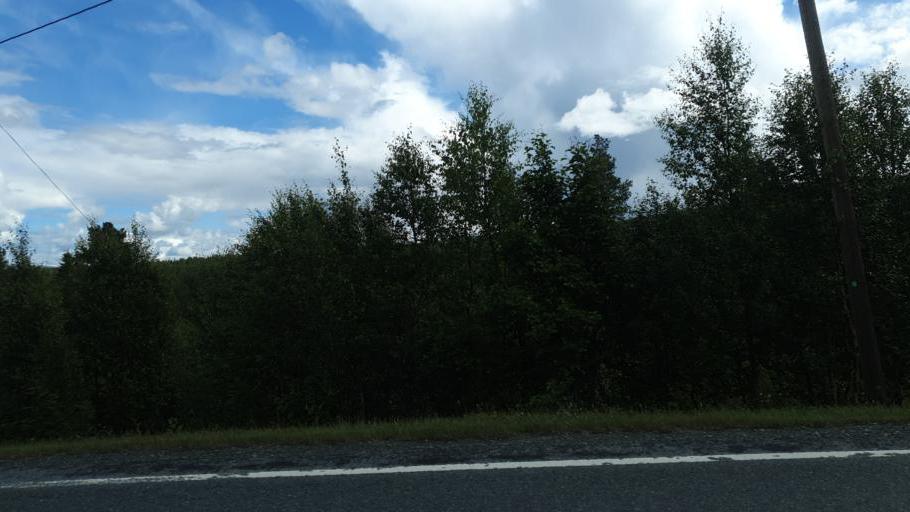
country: NO
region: Sor-Trondelag
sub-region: Rennebu
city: Berkak
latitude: 62.6888
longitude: 9.9326
